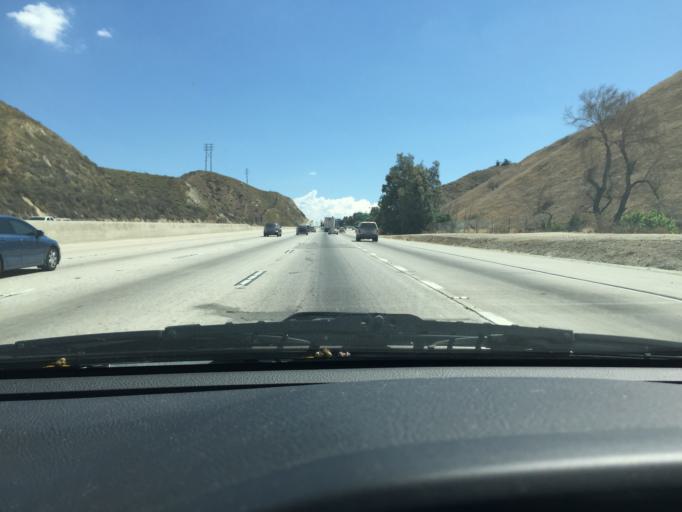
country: US
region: California
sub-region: San Bernardino County
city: Mentone
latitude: 34.0305
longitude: -117.1327
